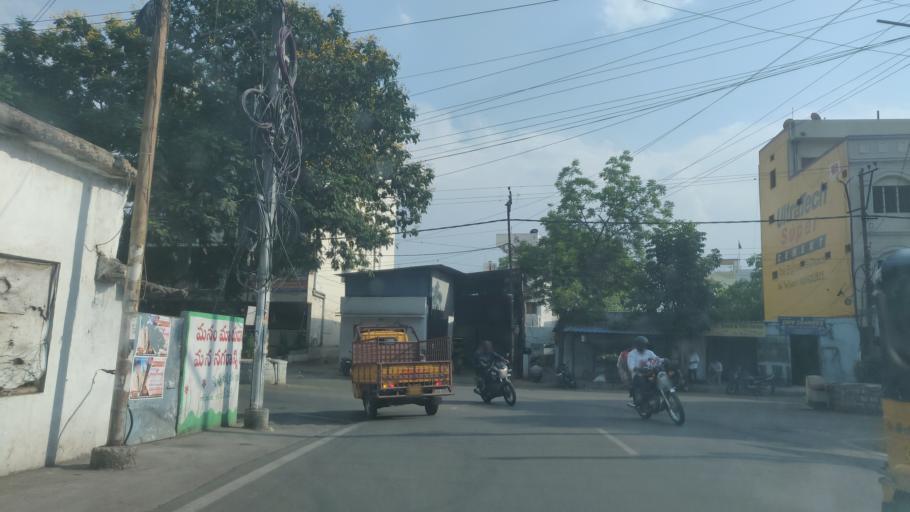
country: IN
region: Telangana
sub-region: Rangareddi
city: Gaddi Annaram
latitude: 17.3878
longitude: 78.5111
